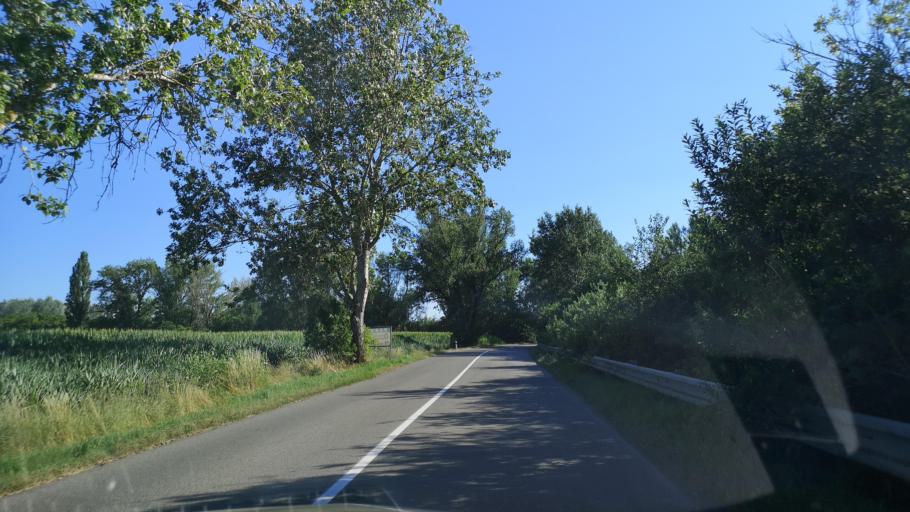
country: SK
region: Trnavsky
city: Dunajska Streda
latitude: 48.0462
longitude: 17.5640
